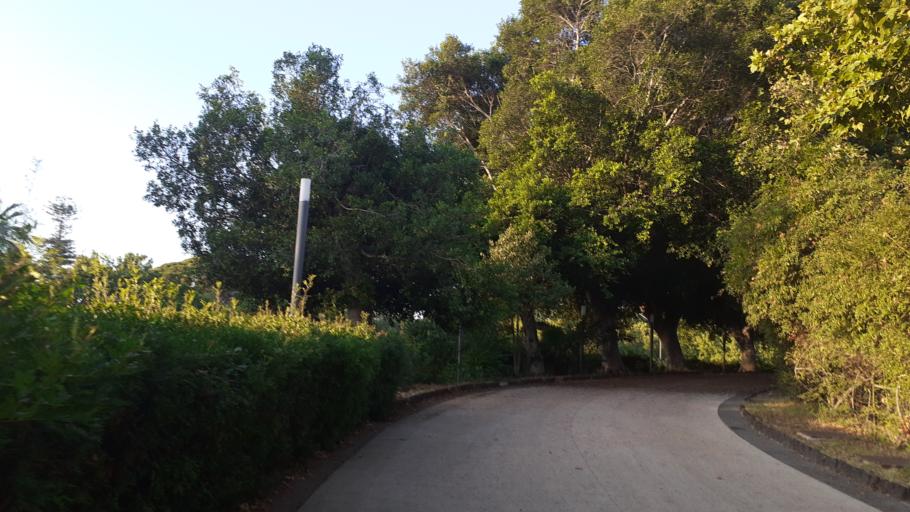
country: IT
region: Sicily
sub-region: Catania
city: Catania
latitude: 37.5120
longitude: 15.0836
